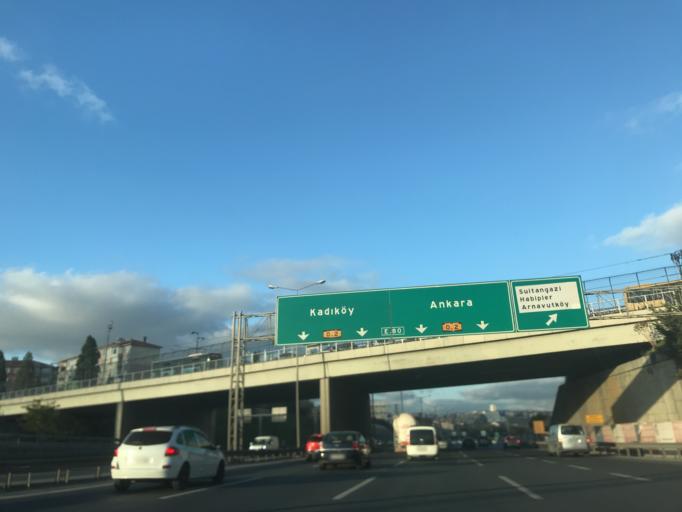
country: TR
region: Istanbul
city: Sultangazi
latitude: 41.0806
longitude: 28.8739
